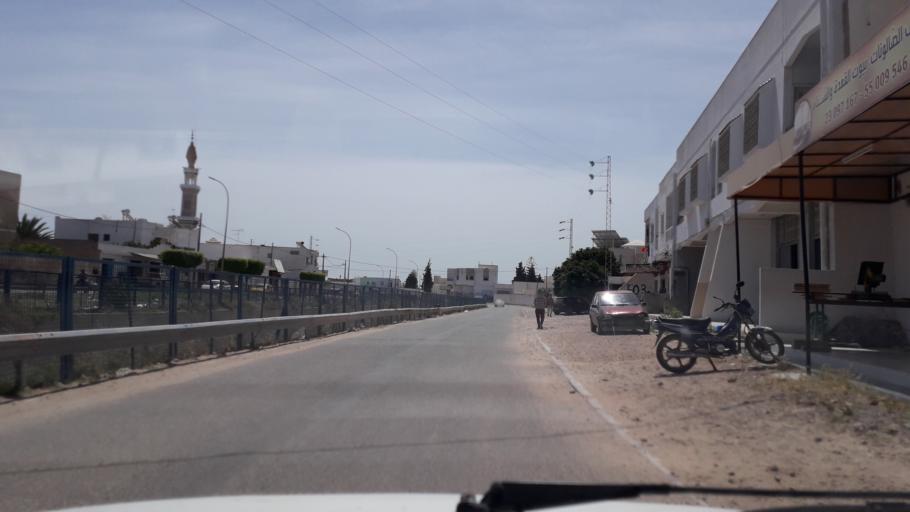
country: TN
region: Safaqis
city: Al Qarmadah
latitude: 34.8008
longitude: 10.7650
